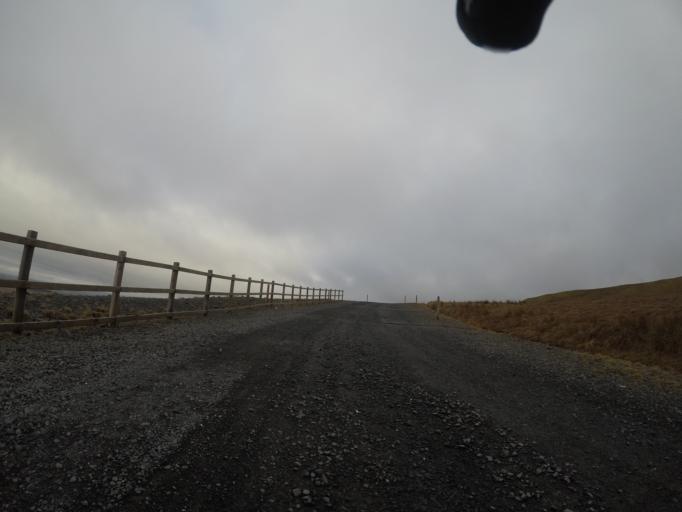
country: GB
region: Scotland
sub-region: North Ayrshire
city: Fairlie
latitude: 55.7631
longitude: -4.7927
